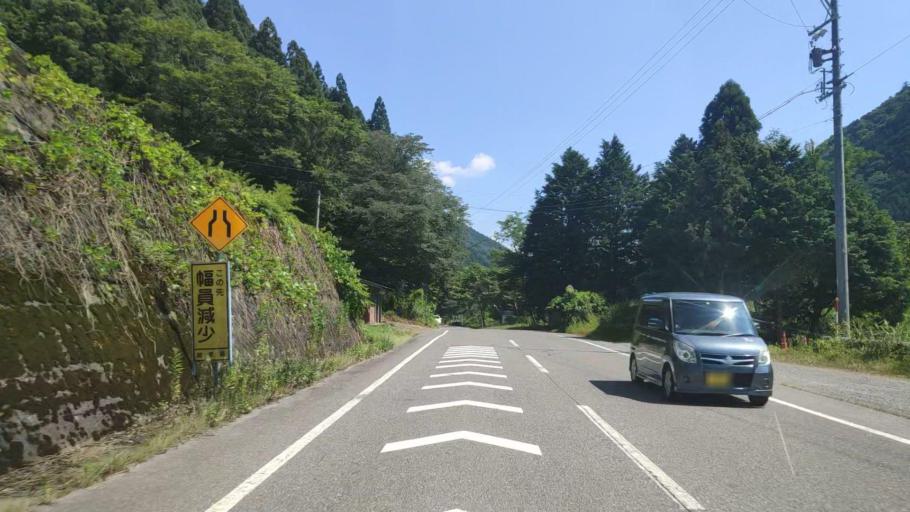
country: JP
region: Gifu
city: Godo
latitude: 35.6134
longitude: 136.6249
